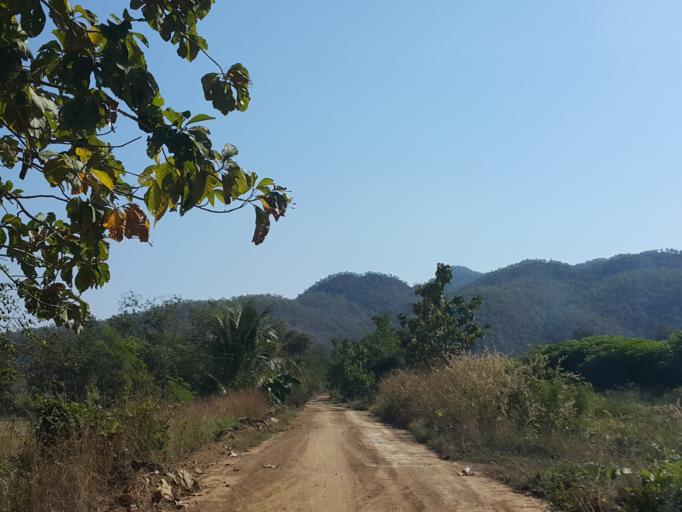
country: TH
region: Sukhothai
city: Thung Saliam
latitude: 17.3218
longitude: 99.4560
